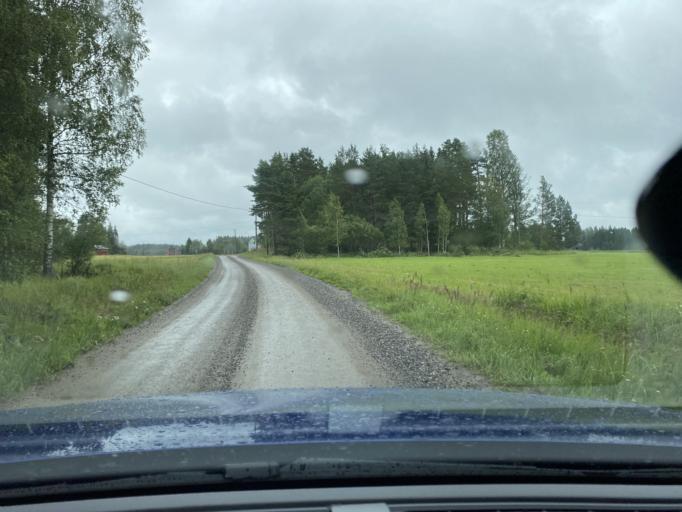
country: FI
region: Pirkanmaa
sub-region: Lounais-Pirkanmaa
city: Punkalaidun
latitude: 61.1456
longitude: 23.2761
